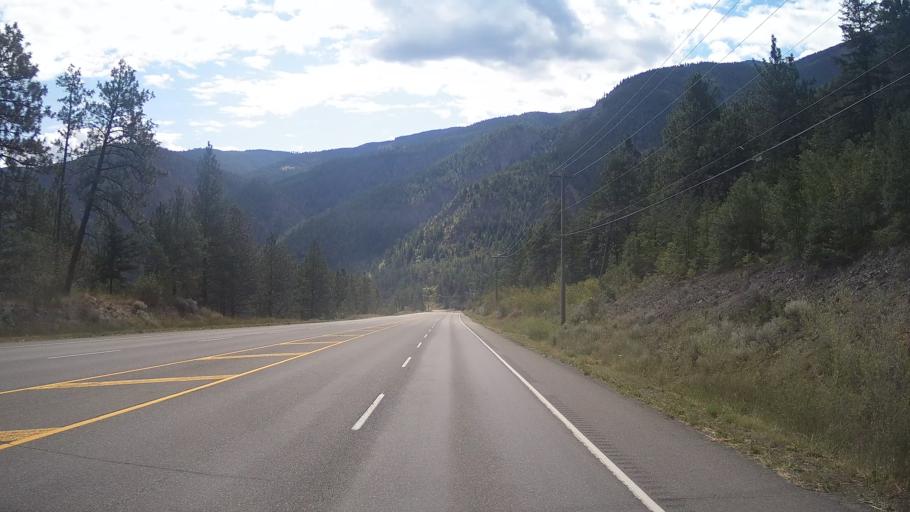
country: CA
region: British Columbia
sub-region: Thompson-Nicola Regional District
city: Ashcroft
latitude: 50.2522
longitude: -121.5065
